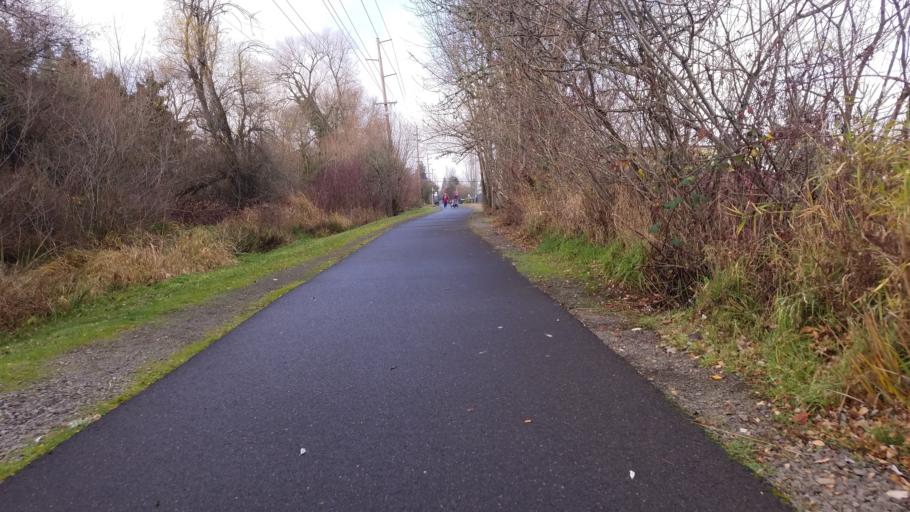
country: US
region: Oregon
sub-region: Clackamas County
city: Jennings Lodge
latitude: 45.3963
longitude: -122.6203
